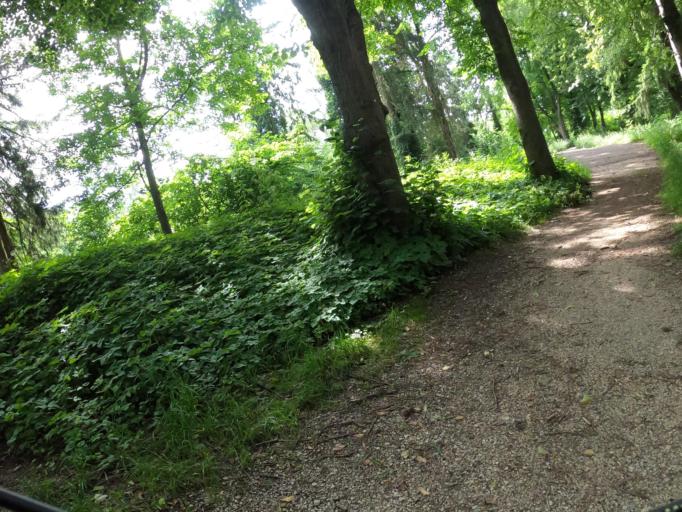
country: DE
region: Baden-Wuerttemberg
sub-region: Tuebingen Region
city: Ulm
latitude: 48.3887
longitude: 9.9942
